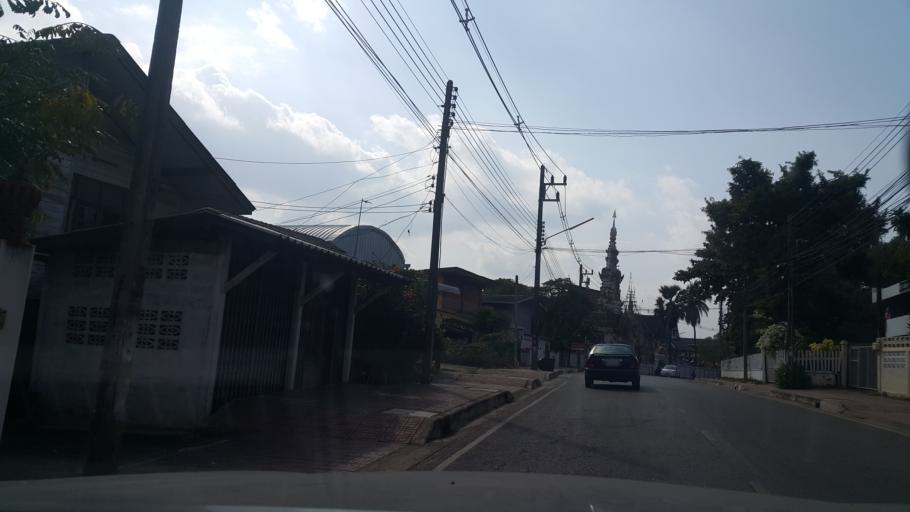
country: TH
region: Phayao
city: Phayao
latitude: 19.1675
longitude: 99.9046
